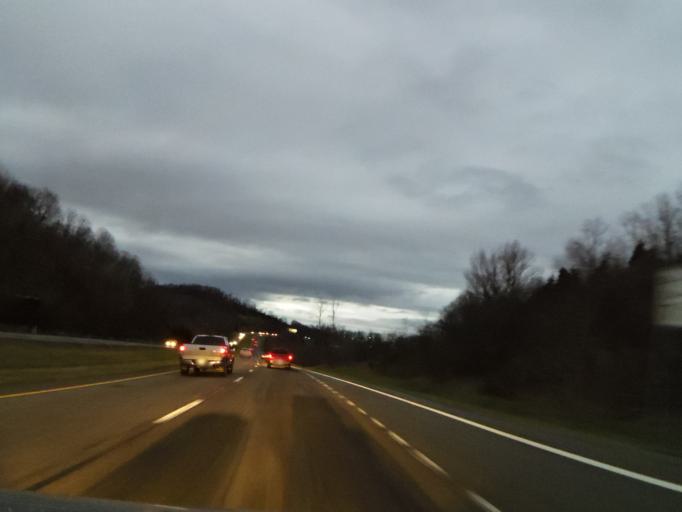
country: US
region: Tennessee
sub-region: Washington County
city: Oak Grove
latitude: 36.3847
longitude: -82.4310
